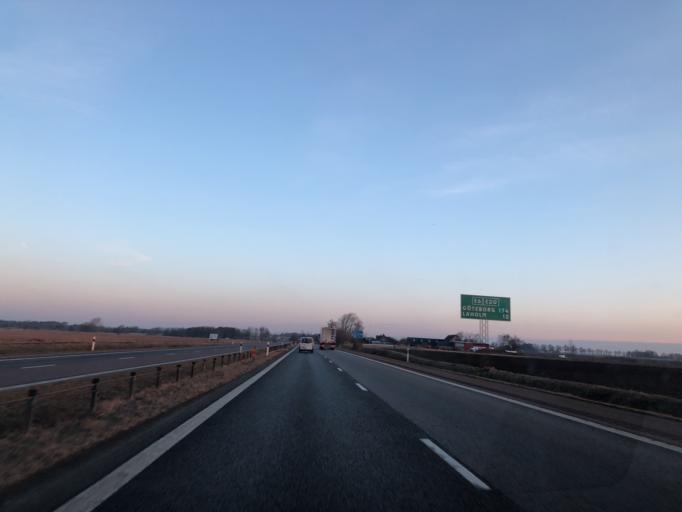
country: SE
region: Halland
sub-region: Laholms Kommun
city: Mellbystrand
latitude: 56.4352
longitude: 12.9534
